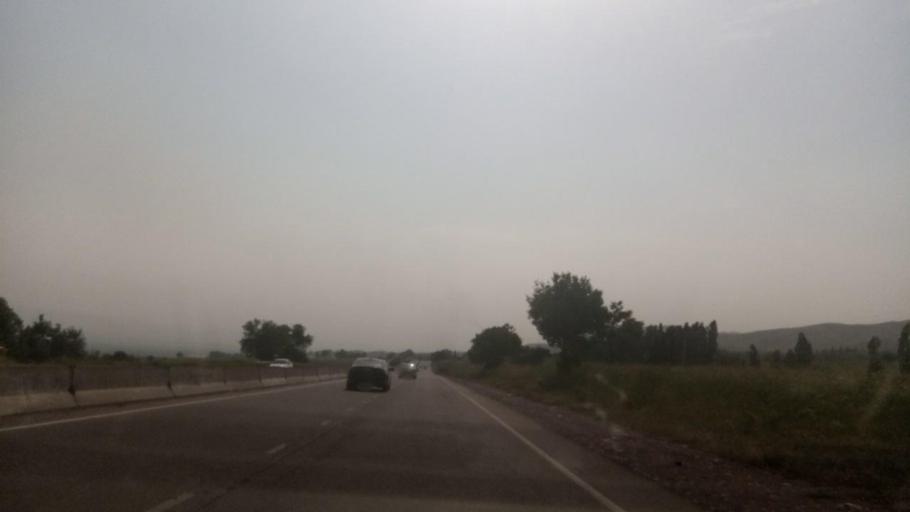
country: UZ
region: Toshkent
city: Angren
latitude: 40.9538
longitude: 69.9239
